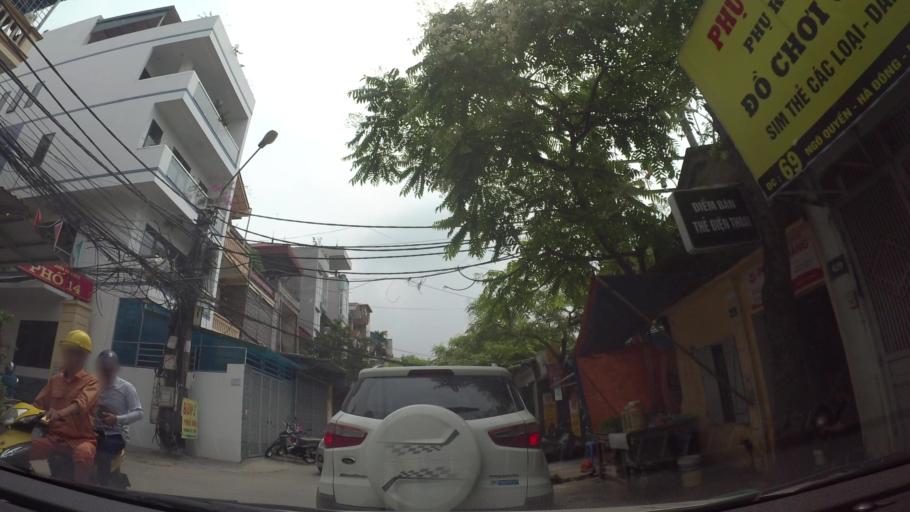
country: VN
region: Ha Noi
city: Ha Dong
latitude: 20.9708
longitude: 105.7656
